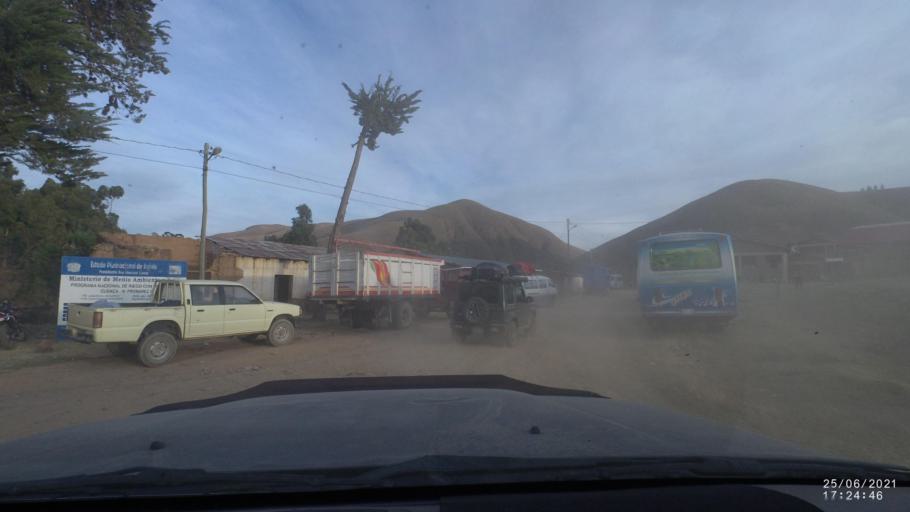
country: BO
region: Cochabamba
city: Mizque
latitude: -17.9144
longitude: -65.6862
